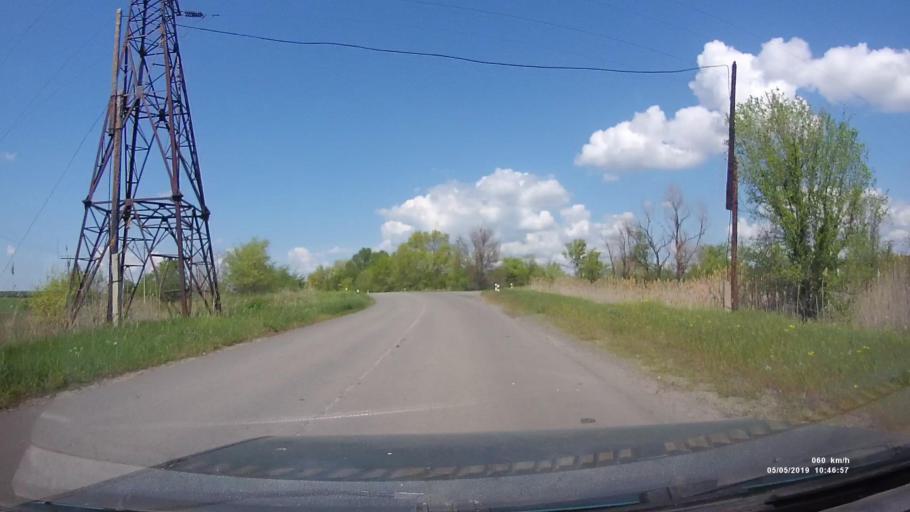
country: RU
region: Rostov
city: Ust'-Donetskiy
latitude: 47.6370
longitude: 40.8388
